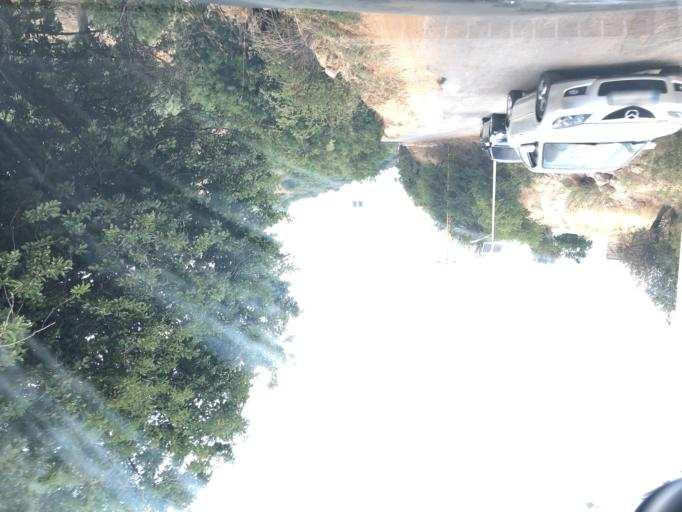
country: LB
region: Liban-Nord
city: Amioun
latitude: 34.1611
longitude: 35.8668
